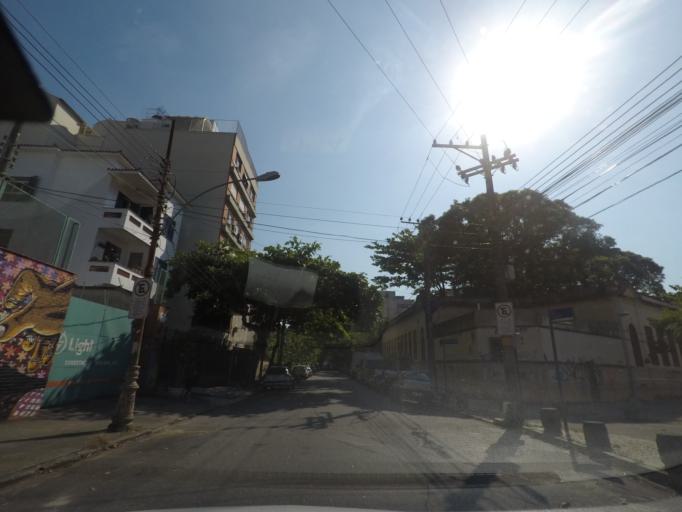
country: BR
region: Rio de Janeiro
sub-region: Rio De Janeiro
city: Rio de Janeiro
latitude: -22.9732
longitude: -43.2274
